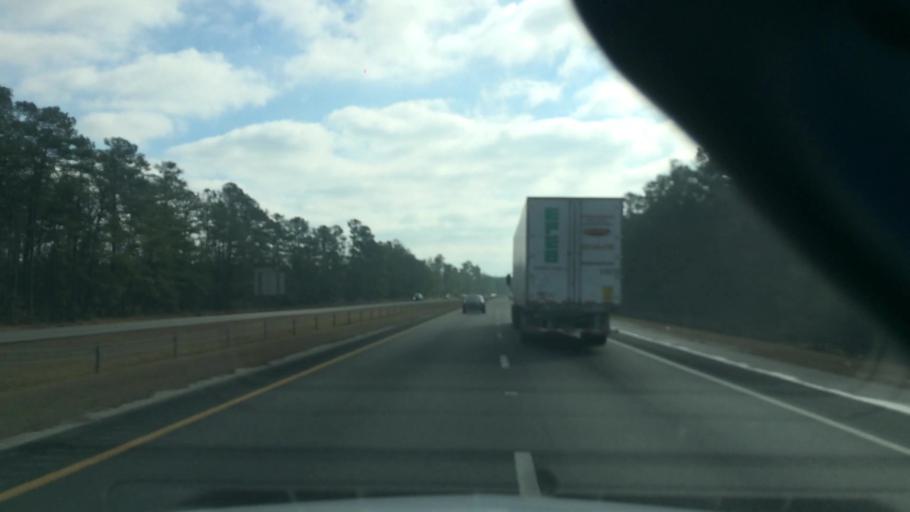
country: US
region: North Carolina
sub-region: Pender County
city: Burgaw
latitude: 34.5581
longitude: -77.8951
